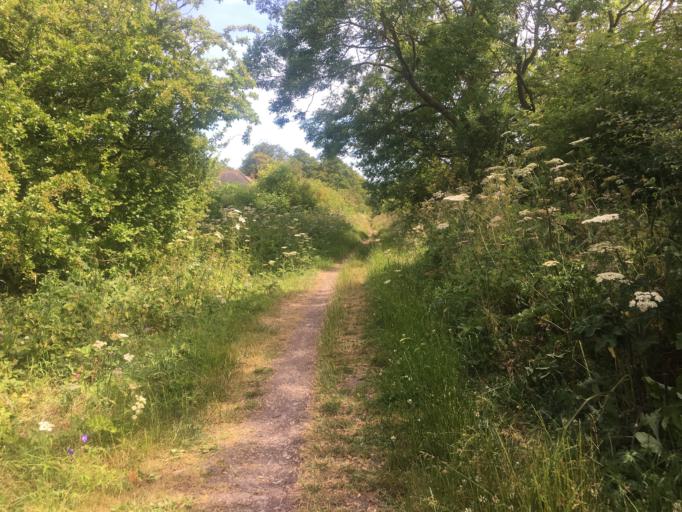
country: GB
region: England
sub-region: Sunderland
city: Washington
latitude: 54.8753
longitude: -1.5389
